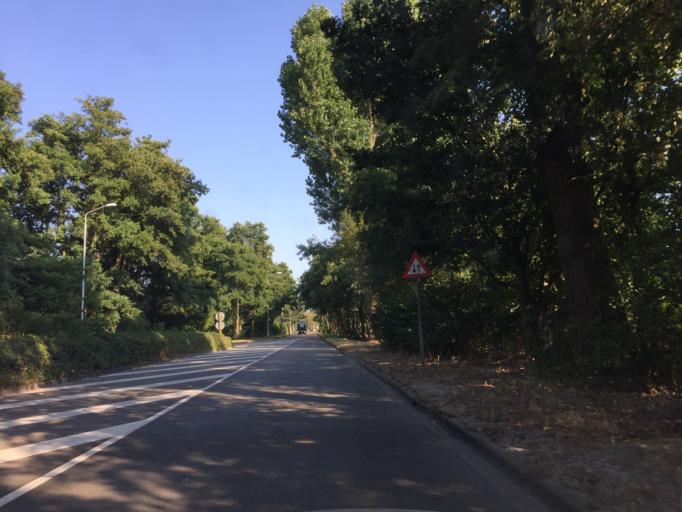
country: NL
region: South Holland
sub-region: Gemeente Wassenaar
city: Wassenaar
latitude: 52.0965
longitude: 4.4082
